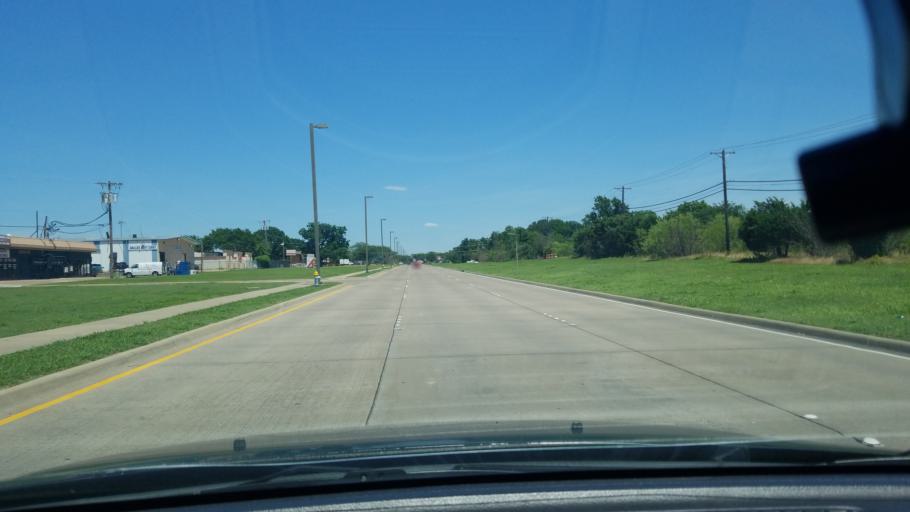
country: US
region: Texas
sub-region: Dallas County
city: Mesquite
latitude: 32.7674
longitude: -96.6161
